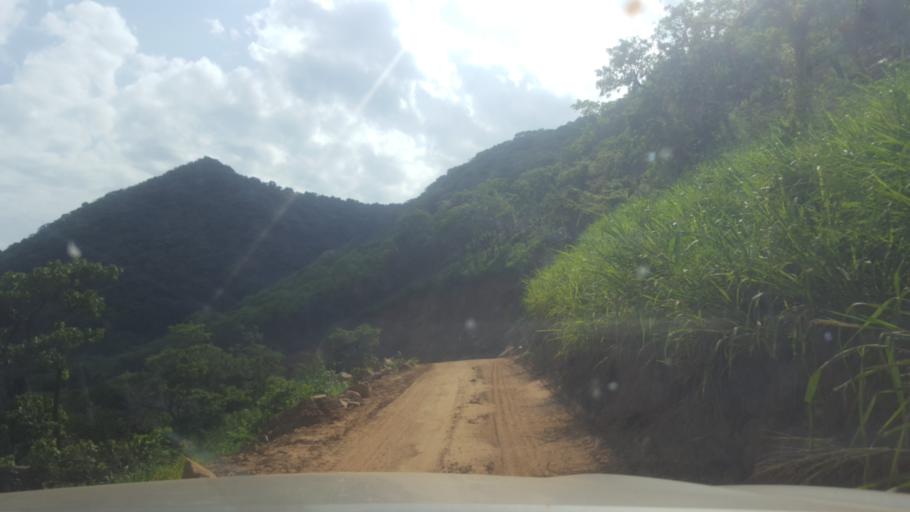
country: ET
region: Southern Nations, Nationalities, and People's Region
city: Tippi
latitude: 7.5362
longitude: 34.9716
